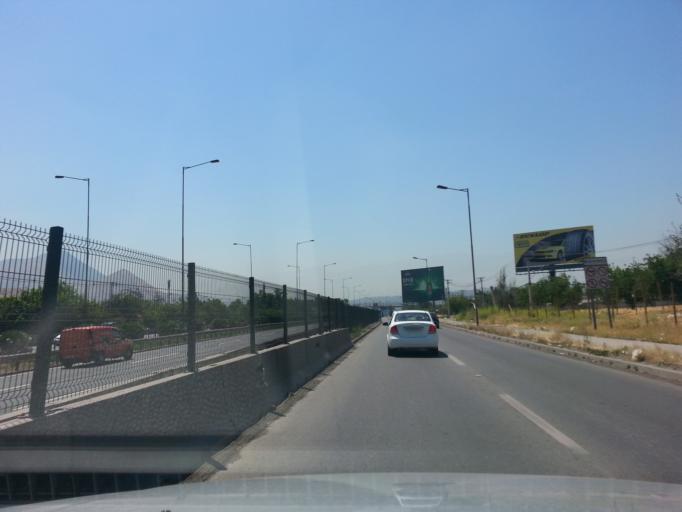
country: CL
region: Santiago Metropolitan
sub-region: Provincia de Santiago
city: Santiago
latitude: -33.3720
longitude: -70.6692
